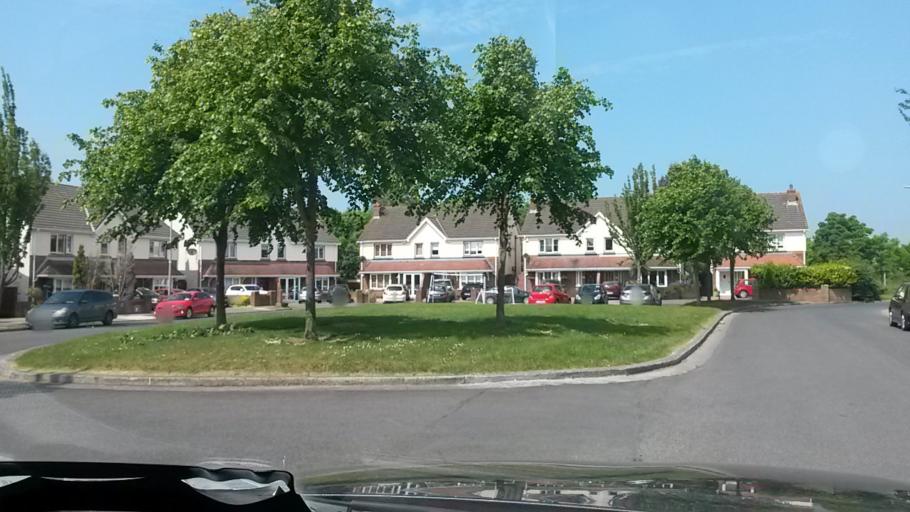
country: IE
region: Leinster
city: Donabate
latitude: 53.4889
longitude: -6.1409
